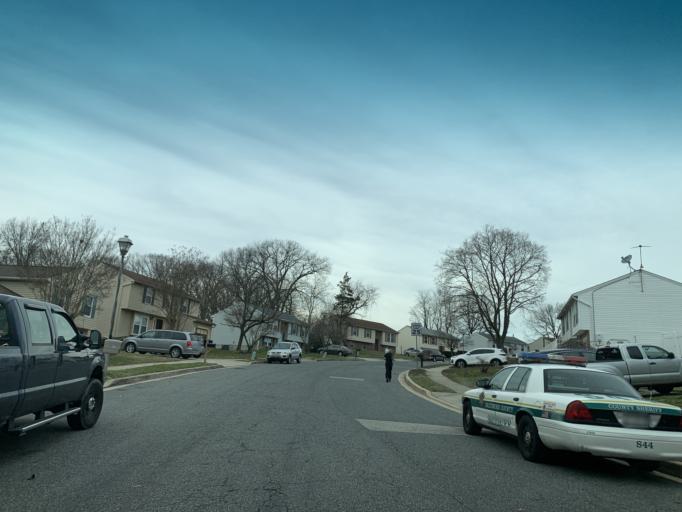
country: US
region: Maryland
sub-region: Baltimore County
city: Rossville
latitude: 39.3309
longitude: -76.4634
